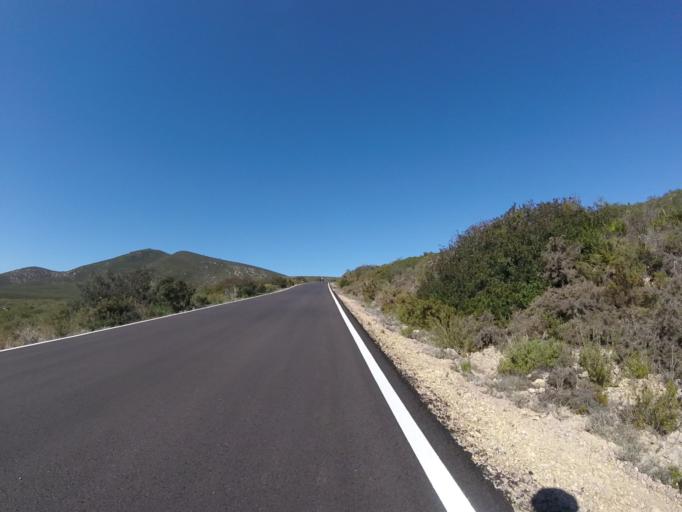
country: ES
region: Valencia
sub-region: Provincia de Castello
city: Cervera del Maestre
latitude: 40.4007
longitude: 0.2330
